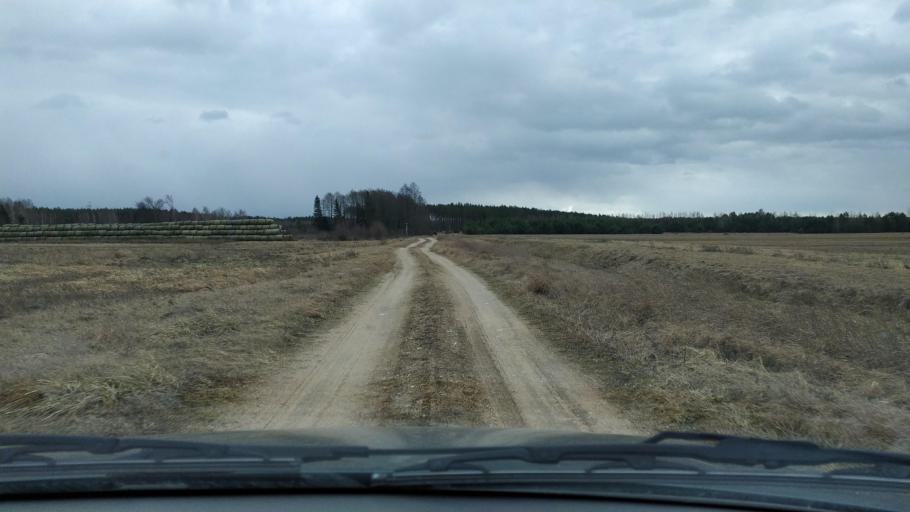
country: BY
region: Brest
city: Zhabinka
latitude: 52.4075
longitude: 24.0684
